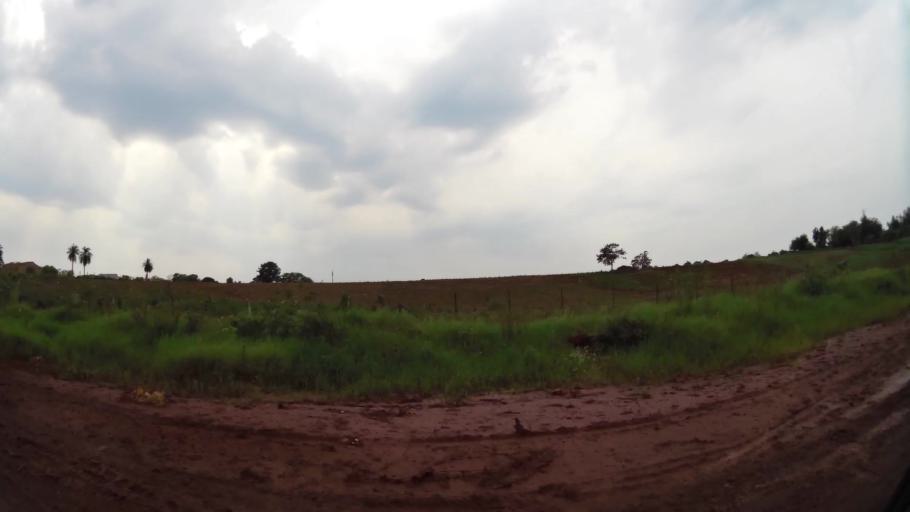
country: PY
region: Alto Parana
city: Presidente Franco
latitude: -25.5440
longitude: -54.6528
